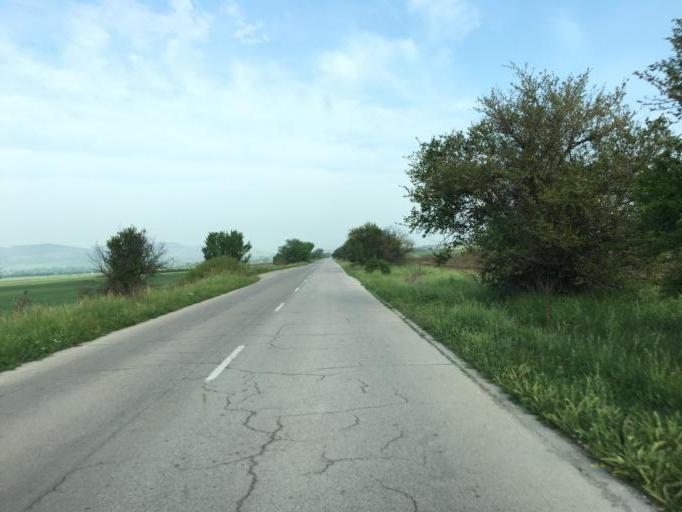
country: BG
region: Kyustendil
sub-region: Obshtina Bobovdol
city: Bobovdol
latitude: 42.4578
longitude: 23.0992
